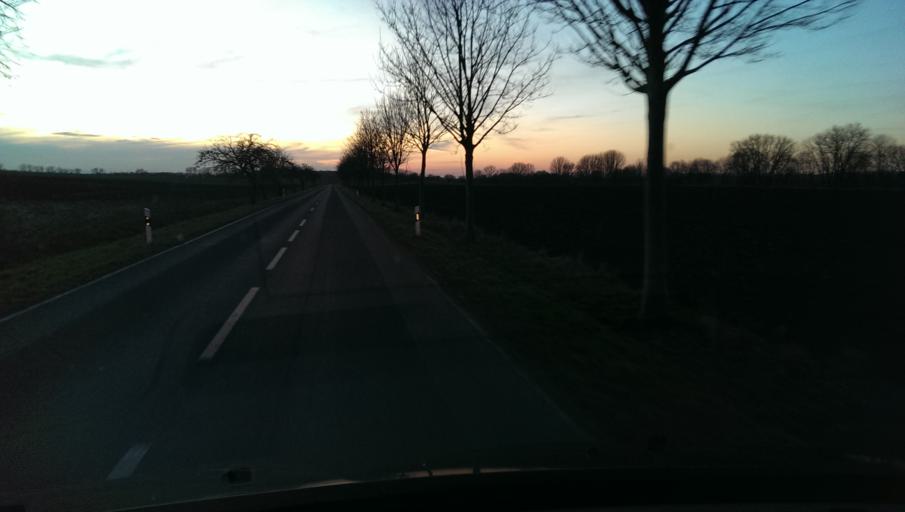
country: DE
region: Saxony-Anhalt
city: Ausleben
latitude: 52.0703
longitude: 11.1197
